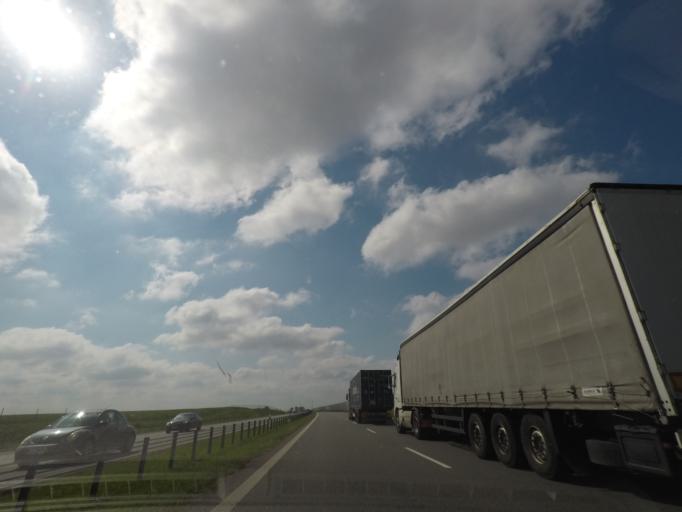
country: PL
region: Kujawsko-Pomorskie
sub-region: Powiat torunski
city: Lubicz Dolny
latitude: 53.1254
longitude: 18.7396
